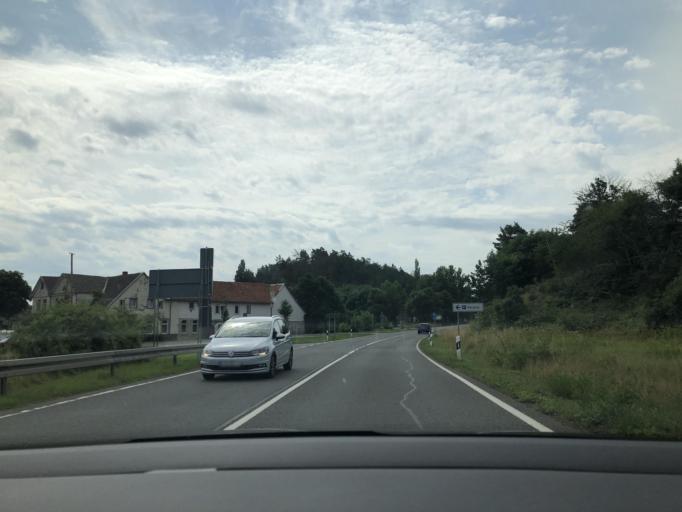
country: DE
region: Saxony-Anhalt
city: Blankenburg
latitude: 51.8240
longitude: 10.9321
